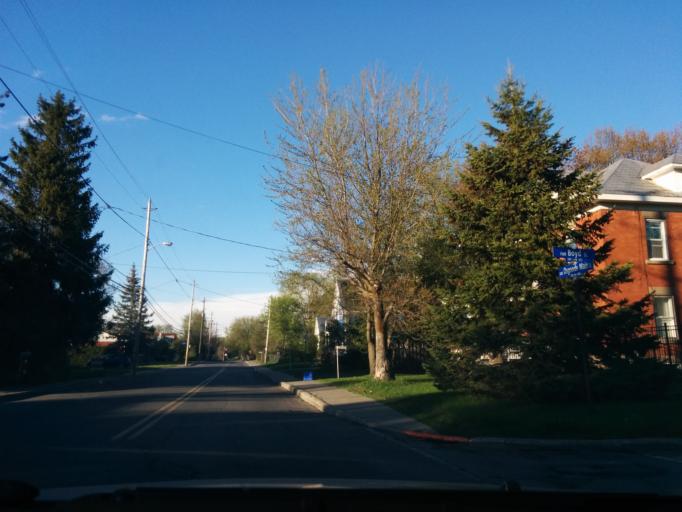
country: CA
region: Ontario
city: Bells Corners
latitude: 45.1415
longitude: -75.6140
